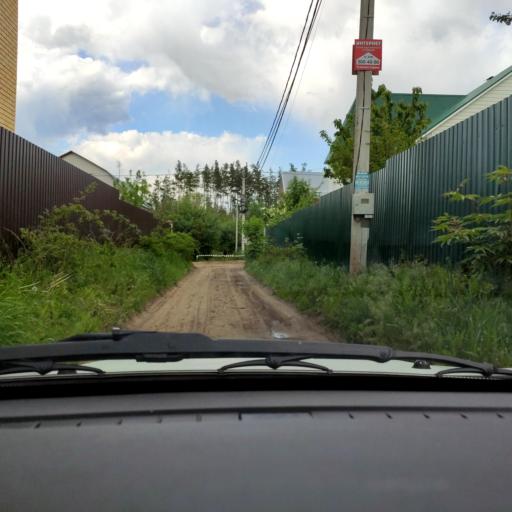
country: RU
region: Voronezj
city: Podgornoye
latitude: 51.7467
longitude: 39.1501
